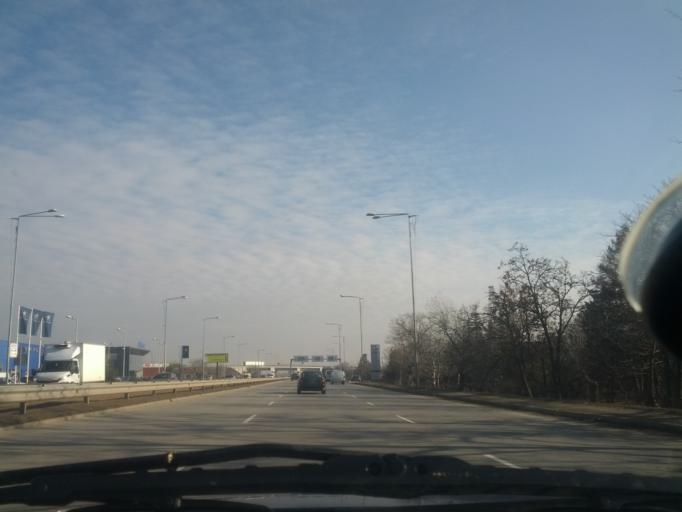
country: BG
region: Sofia-Capital
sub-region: Stolichna Obshtina
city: Sofia
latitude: 42.7088
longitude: 23.4331
